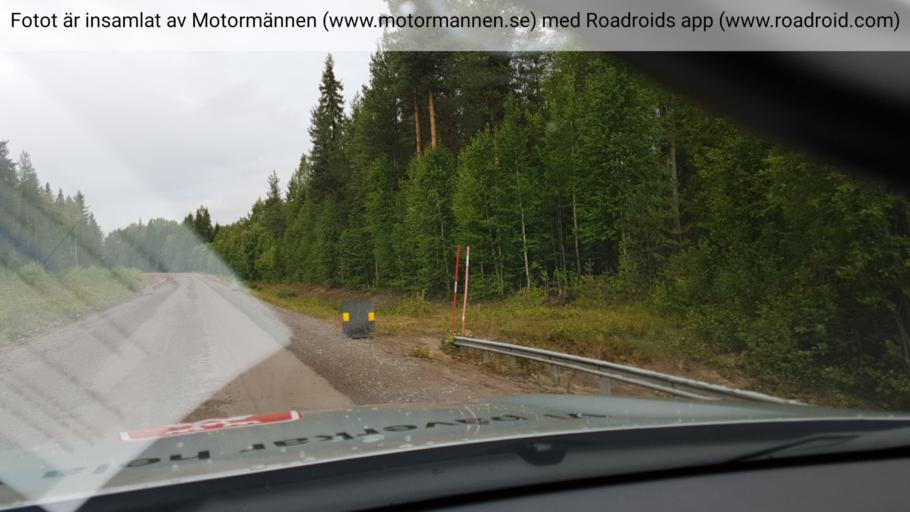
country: SE
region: Norrbotten
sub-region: Alvsbyns Kommun
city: AElvsbyn
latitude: 66.0107
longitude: 21.0909
